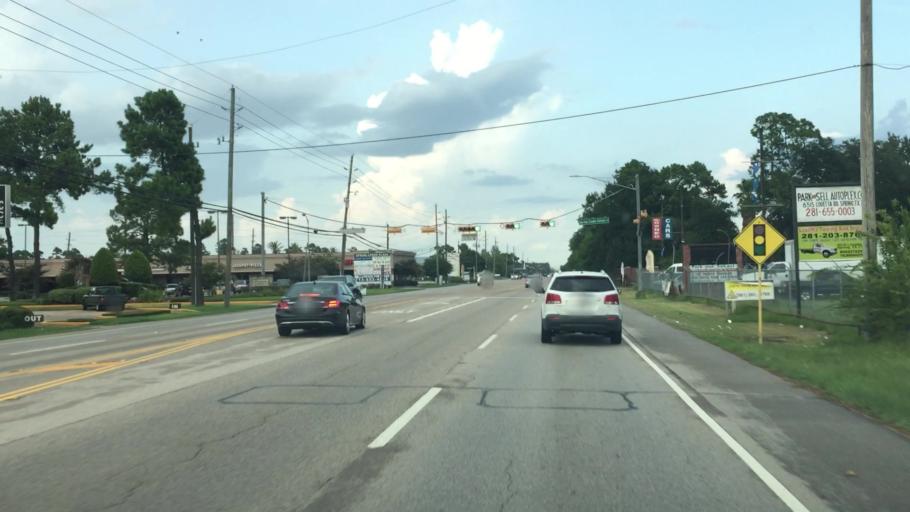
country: US
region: Texas
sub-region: Harris County
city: Spring
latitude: 30.0263
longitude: -95.5141
